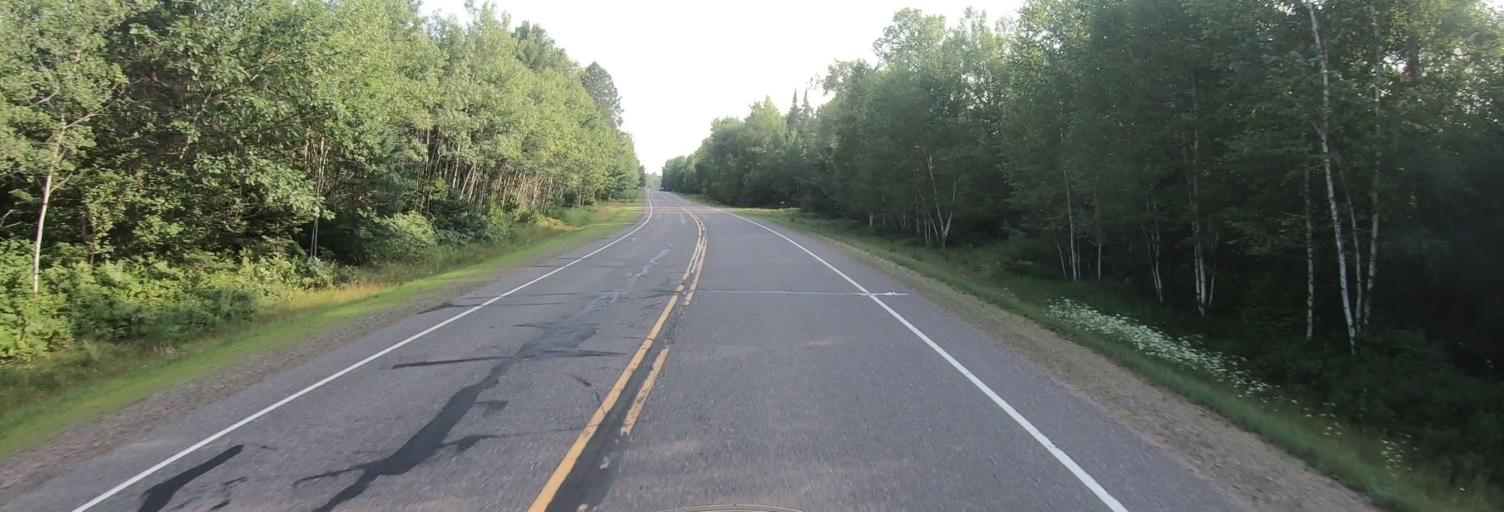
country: US
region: Wisconsin
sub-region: Ashland County
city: Ashland
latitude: 46.1625
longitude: -90.9134
